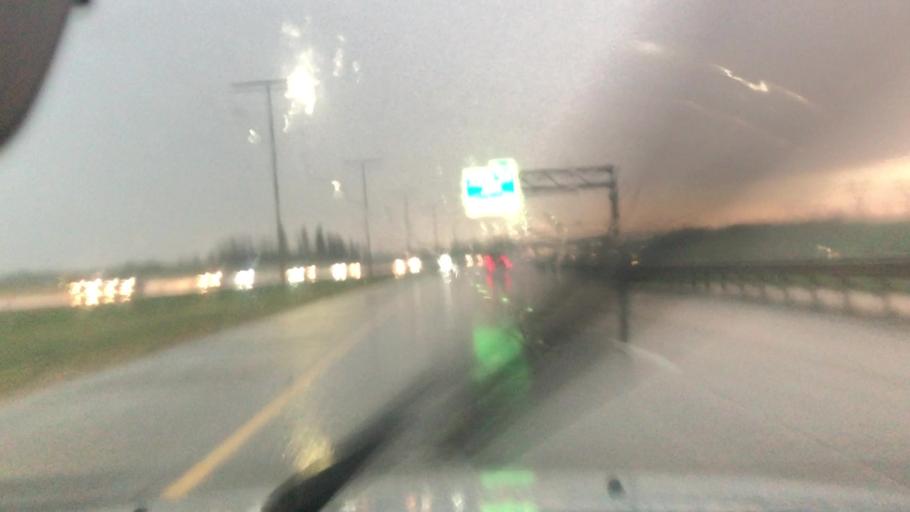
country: CA
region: Alberta
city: Edmonton
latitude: 53.4302
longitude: -113.5542
